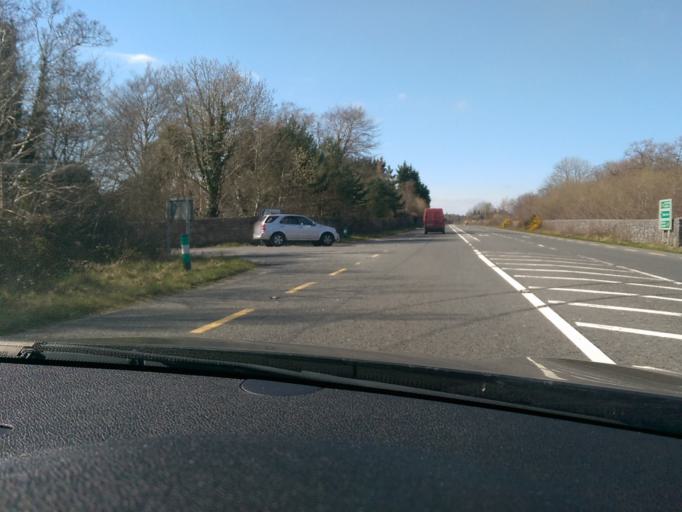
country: IE
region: Connaught
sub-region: County Galway
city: Moycullen
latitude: 53.3133
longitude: -9.1473
